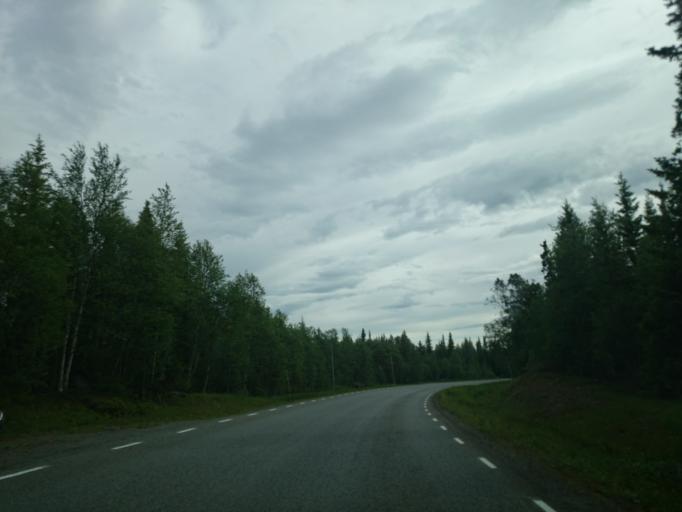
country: SE
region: Jaemtland
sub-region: Are Kommun
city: Are
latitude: 63.2072
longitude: 13.1622
